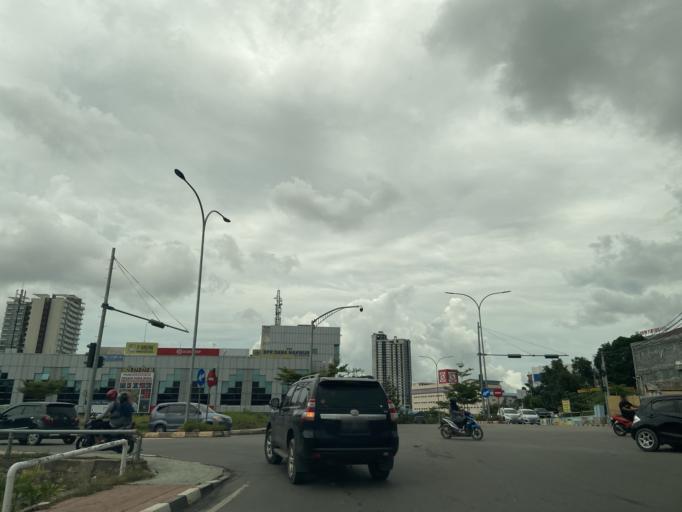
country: SG
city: Singapore
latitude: 1.1452
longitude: 104.0175
